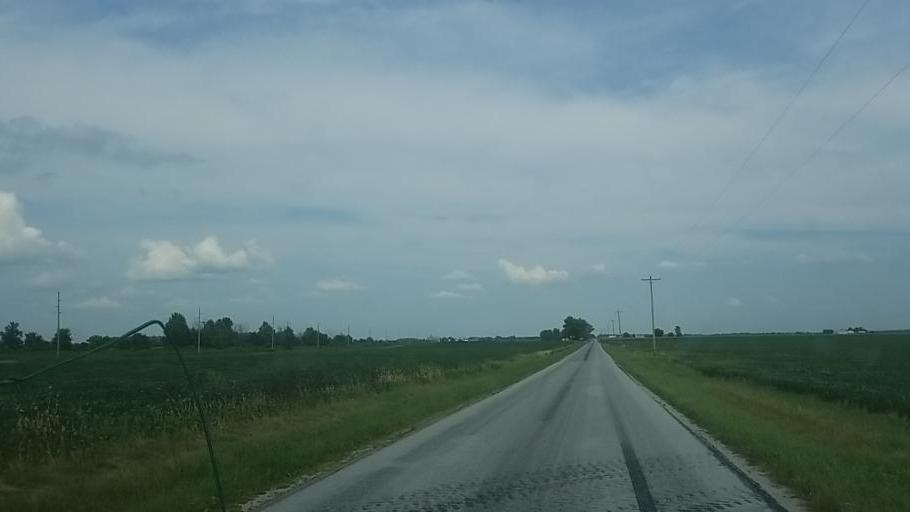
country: US
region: Ohio
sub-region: Wyandot County
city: Upper Sandusky
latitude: 40.8178
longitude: -83.3504
